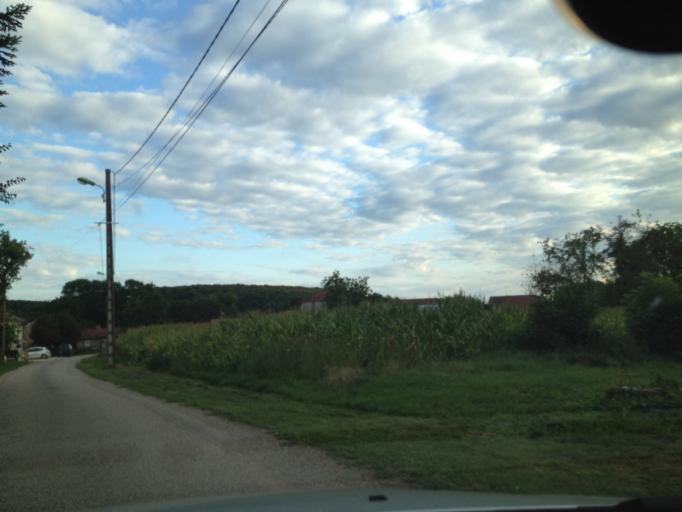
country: FR
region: Lorraine
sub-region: Departement des Vosges
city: Bains-les-Bains
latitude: 47.9748
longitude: 6.1768
